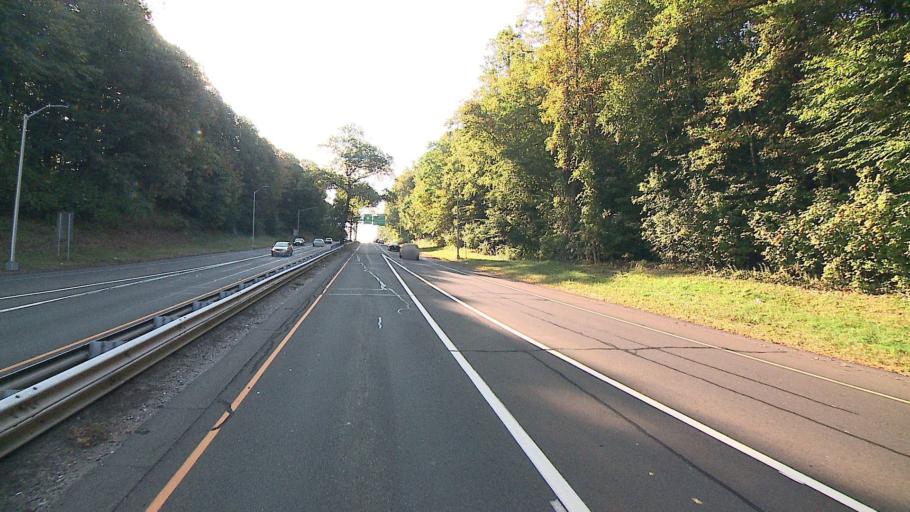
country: US
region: Connecticut
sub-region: New Haven County
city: City of Milford (balance)
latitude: 41.2453
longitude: -73.0836
